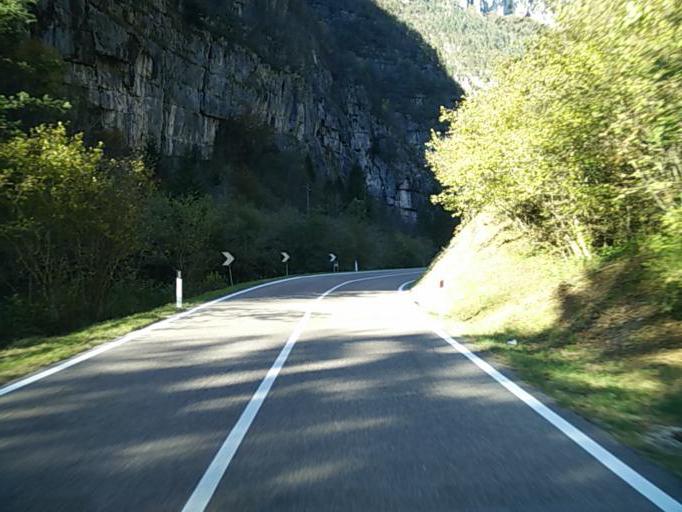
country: IT
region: Trentino-Alto Adige
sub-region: Provincia di Trento
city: Condino
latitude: 45.8552
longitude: 10.6369
